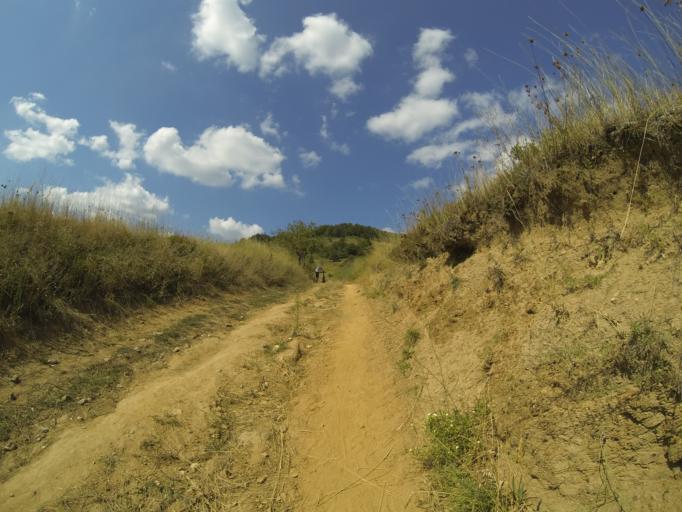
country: RO
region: Mehedinti
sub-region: Comuna Svinita
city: Svinita
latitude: 44.5572
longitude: 22.1385
